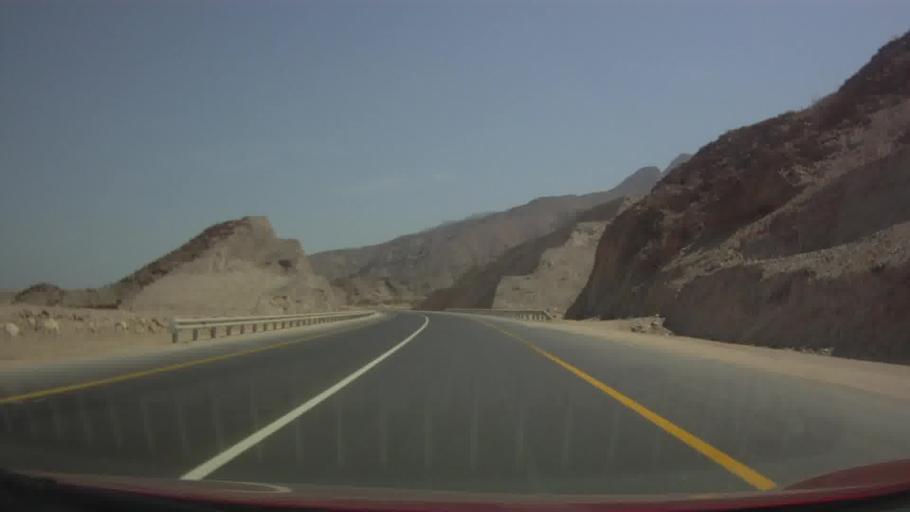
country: OM
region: Muhafazat Masqat
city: Muscat
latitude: 23.3971
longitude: 58.7836
